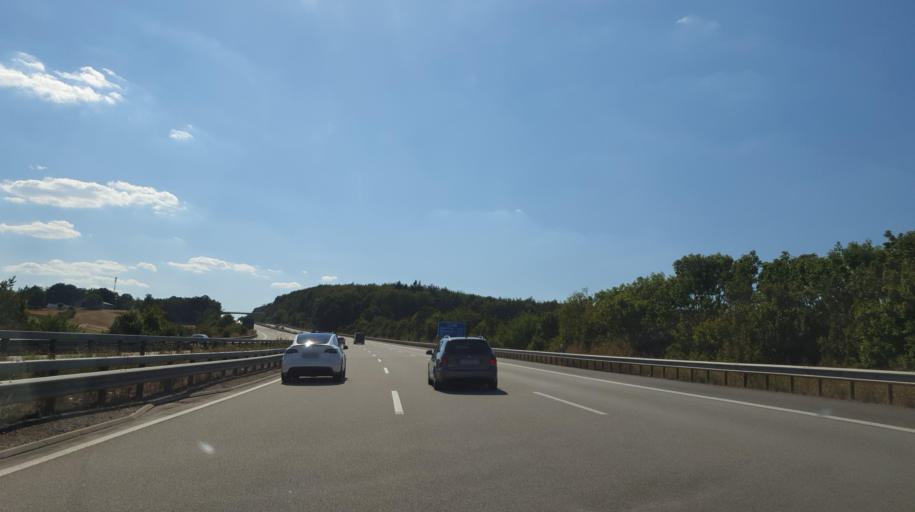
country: DE
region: Rheinland-Pfalz
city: Wattenheim
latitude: 49.5268
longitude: 8.0566
